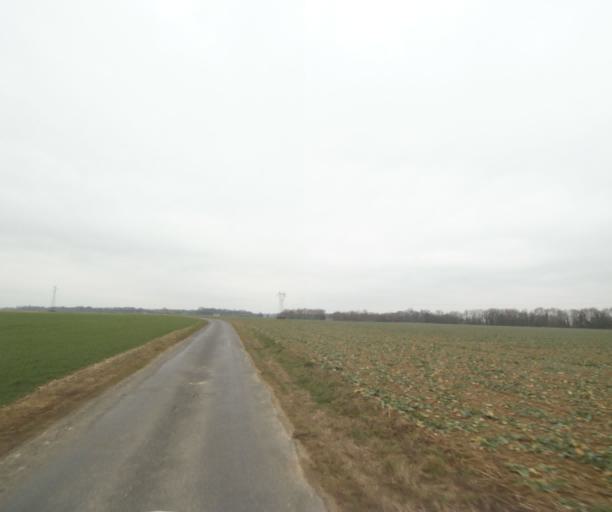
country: FR
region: Champagne-Ardenne
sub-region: Departement de la Haute-Marne
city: Villiers-en-Lieu
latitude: 48.6337
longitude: 4.8289
